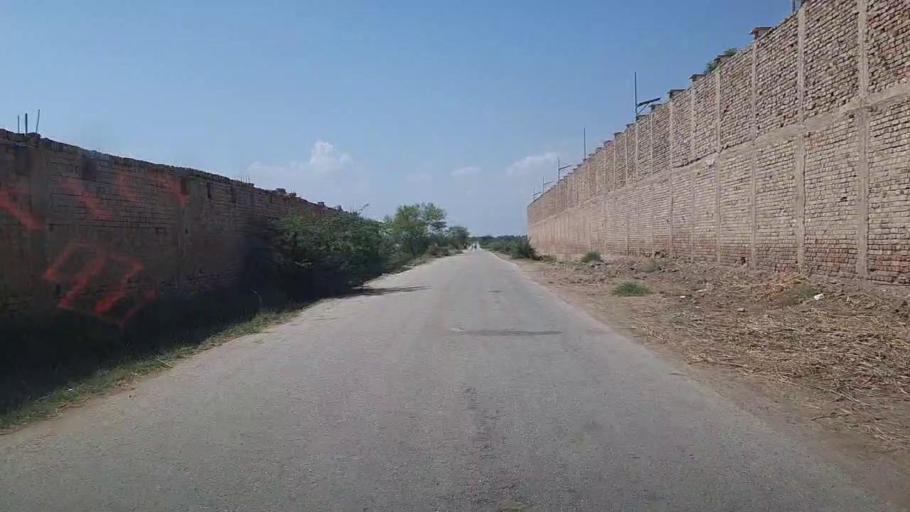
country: PK
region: Sindh
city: Khairpur
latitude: 28.0670
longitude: 69.6436
